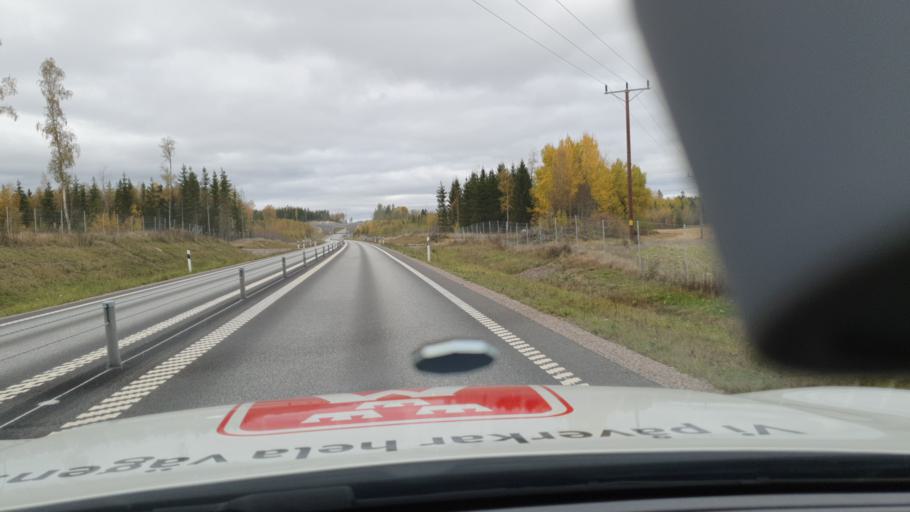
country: SE
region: OErebro
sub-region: Hallsbergs Kommun
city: Palsboda
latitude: 59.0456
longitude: 15.3428
